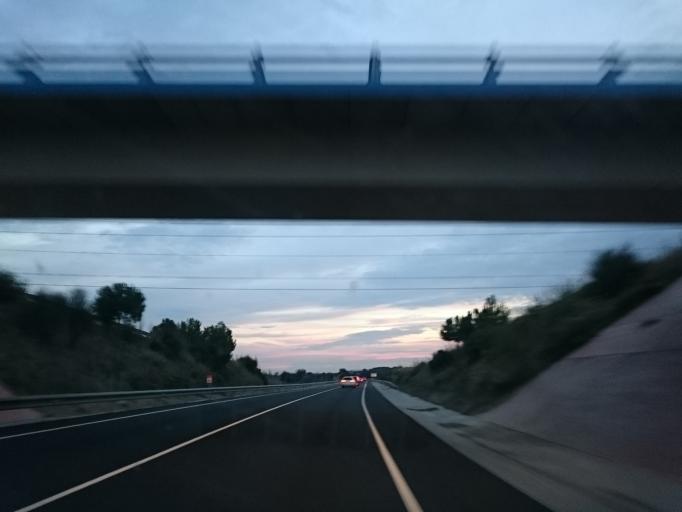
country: ES
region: Catalonia
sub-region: Provincia de Barcelona
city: Sant Pere de Riudebitlles
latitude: 41.4412
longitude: 1.6851
